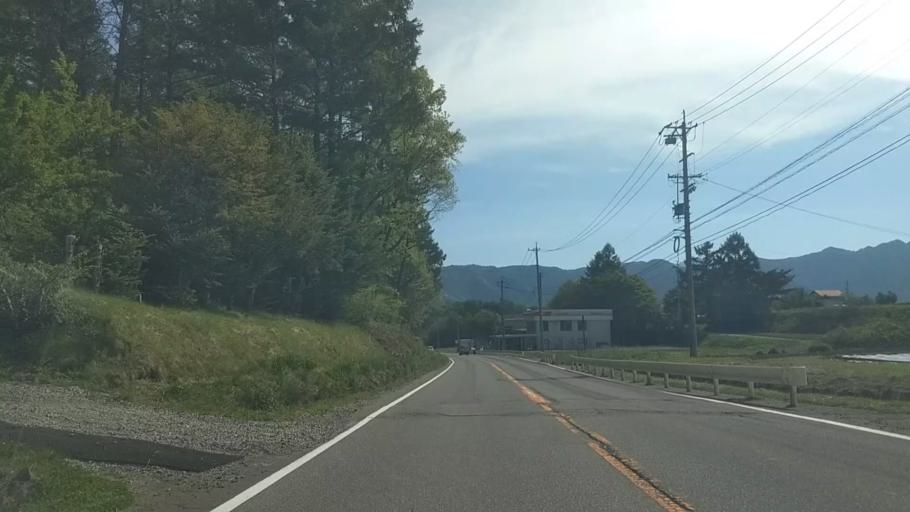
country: JP
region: Nagano
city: Saku
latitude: 36.0008
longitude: 138.5017
